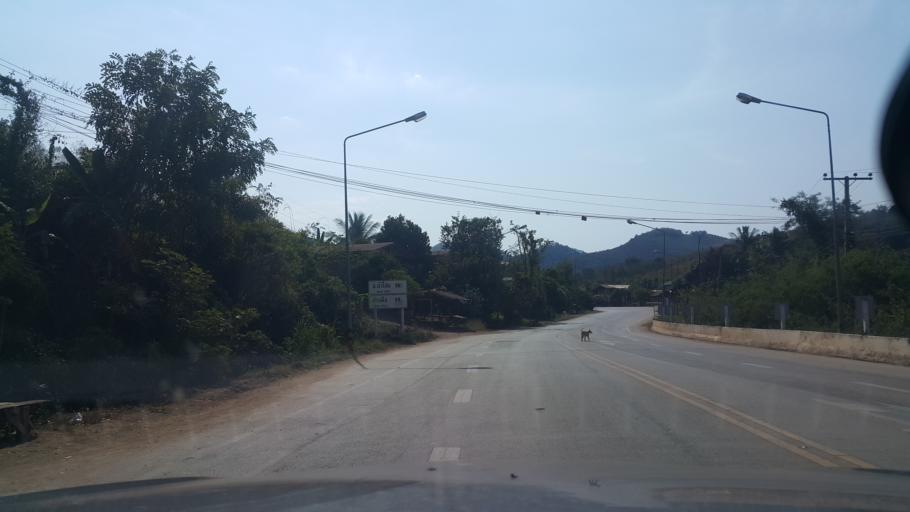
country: TH
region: Loei
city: Pak Chom
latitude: 18.1191
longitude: 101.9972
